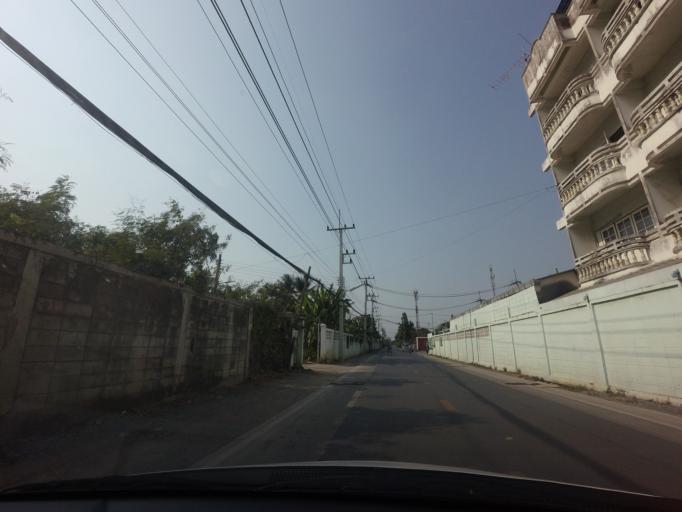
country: TH
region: Nakhon Pathom
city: Sam Phran
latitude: 13.6971
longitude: 100.2455
